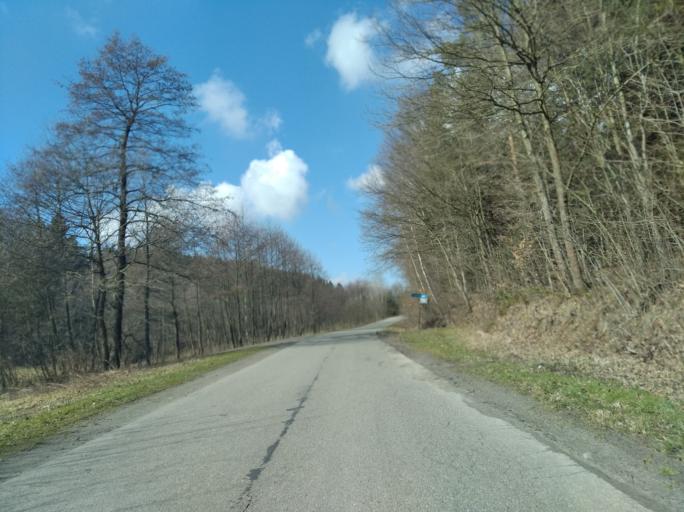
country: PL
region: Subcarpathian Voivodeship
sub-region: Powiat strzyzowski
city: Frysztak
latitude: 49.8645
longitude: 21.5459
